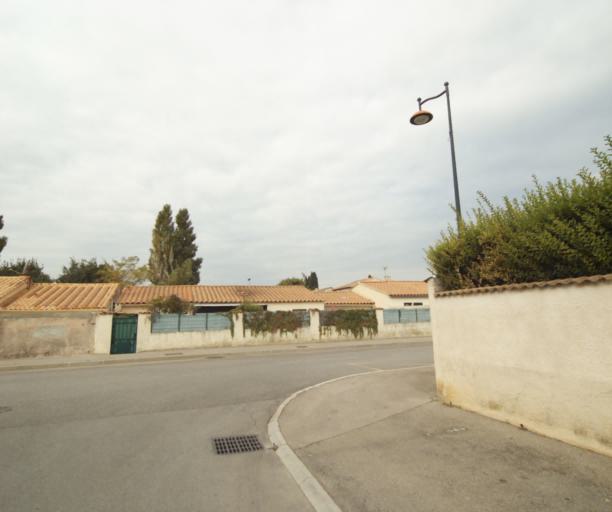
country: FR
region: Provence-Alpes-Cote d'Azur
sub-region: Departement des Bouches-du-Rhone
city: Saint-Victoret
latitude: 43.4160
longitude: 5.2575
